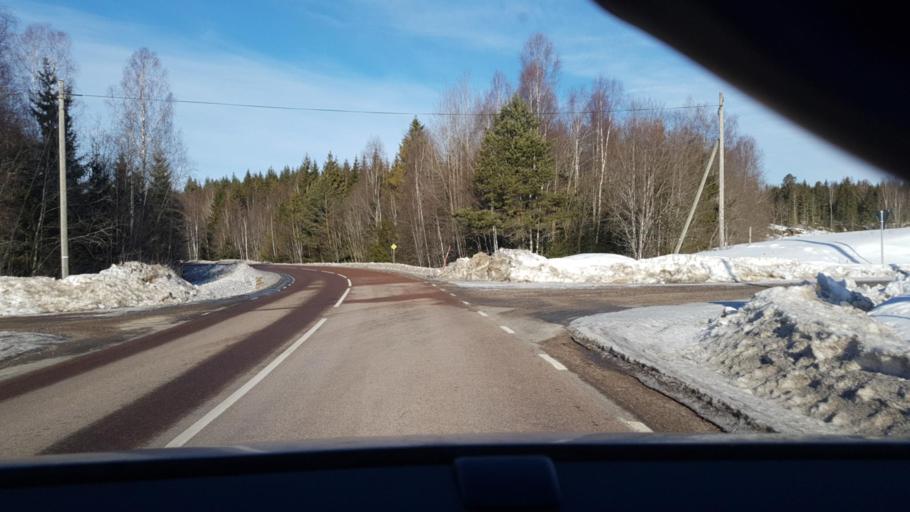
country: SE
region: Vaermland
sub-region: Eda Kommun
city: Charlottenberg
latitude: 59.8111
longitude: 12.1854
